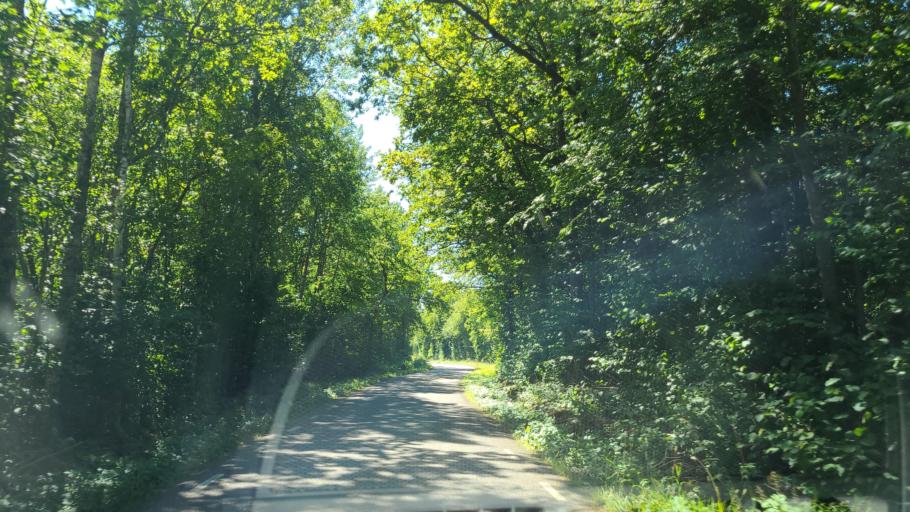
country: SE
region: Kalmar
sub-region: Borgholms Kommun
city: Borgholm
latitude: 56.7529
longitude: 16.6589
